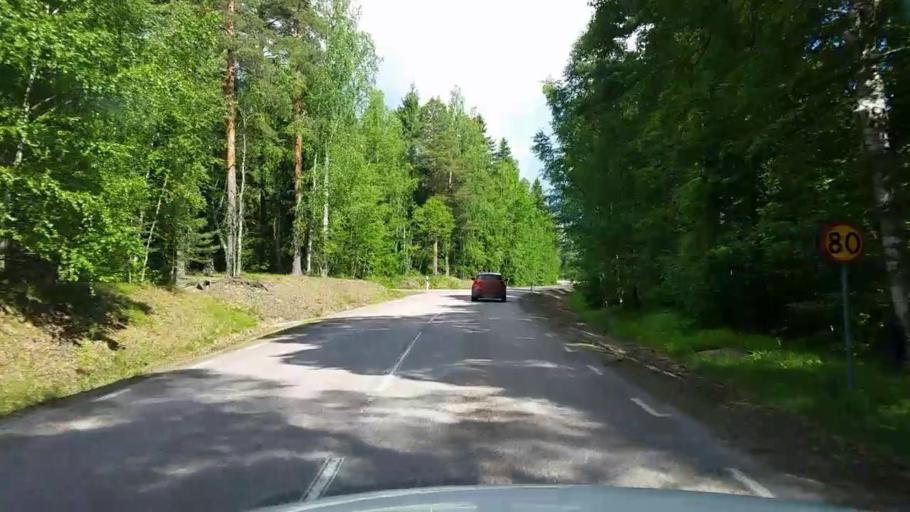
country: SE
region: Vaestmanland
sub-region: Skinnskattebergs Kommun
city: Skinnskatteberg
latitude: 59.7830
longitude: 15.8598
